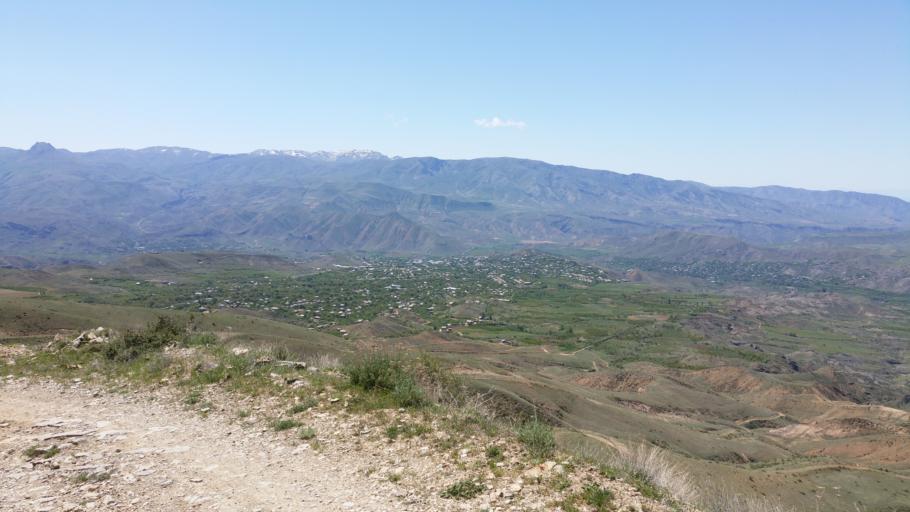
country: AM
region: Vayots' Dzori Marz
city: Vernashen
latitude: 39.8035
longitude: 45.3588
